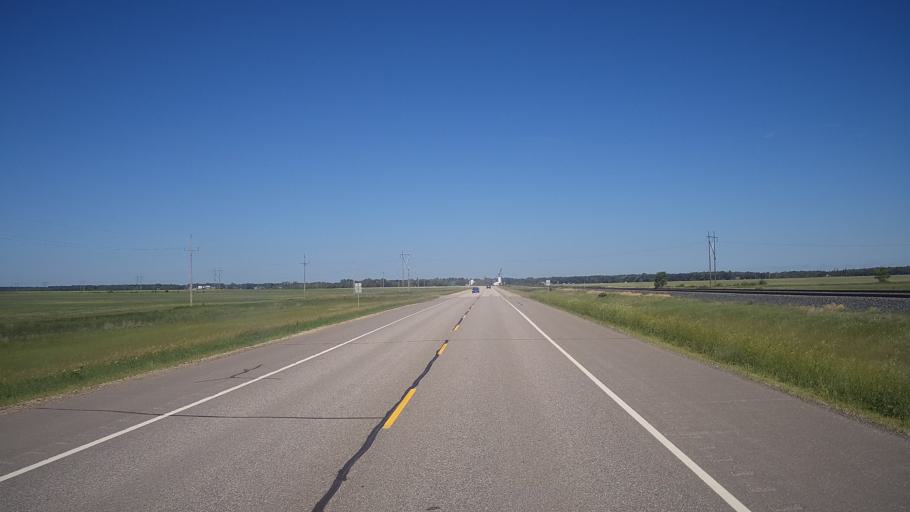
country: CA
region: Manitoba
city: Portage la Prairie
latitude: 50.1204
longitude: -98.5626
